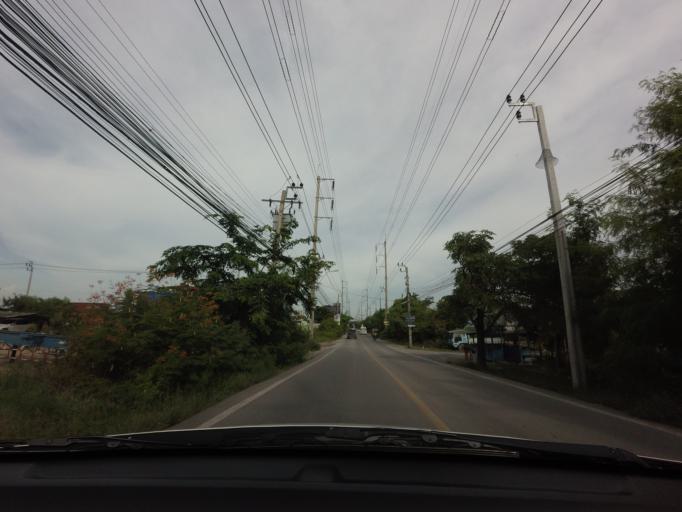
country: TH
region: Bangkok
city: Bang Na
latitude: 13.6192
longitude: 100.6583
